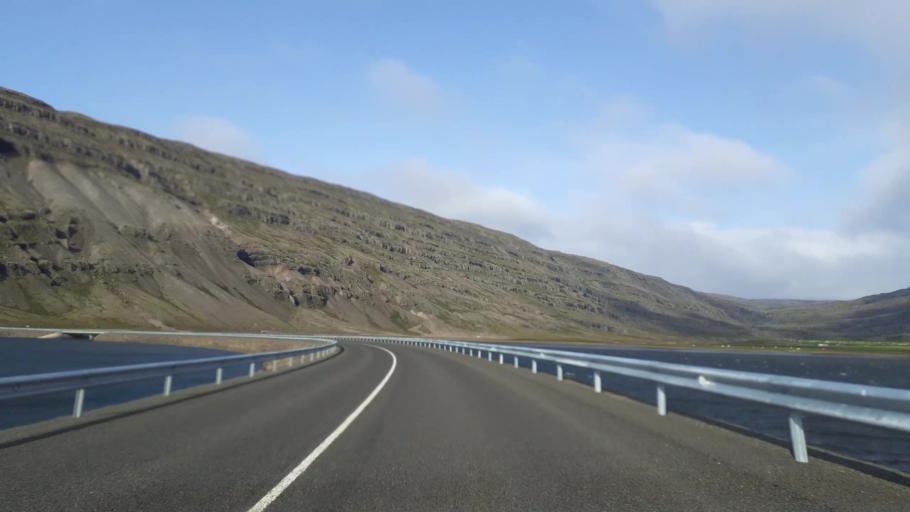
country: IS
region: East
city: Reydarfjoerdur
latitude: 64.7904
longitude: -14.4816
